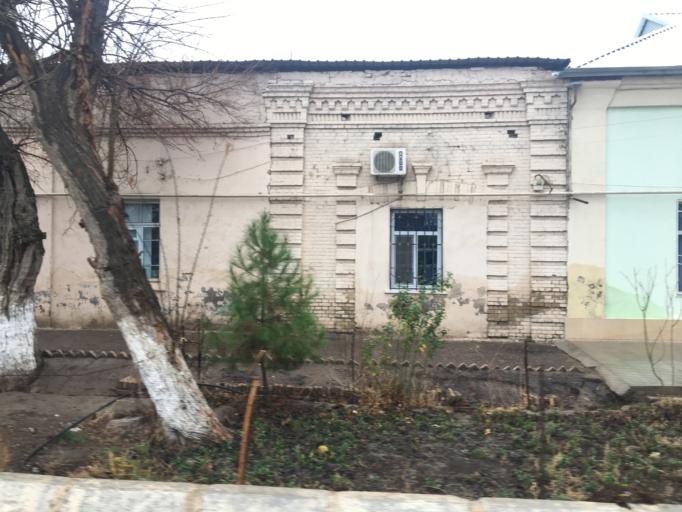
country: TM
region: Mary
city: Yoloeten
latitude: 37.3007
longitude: 62.3597
